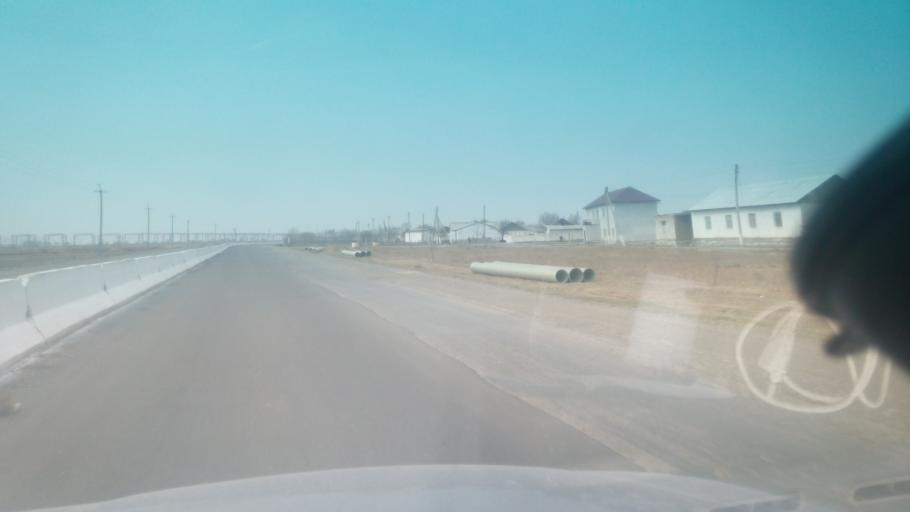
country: TJ
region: Viloyati Sughd
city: Zafarobod
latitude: 40.2185
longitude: 68.8183
